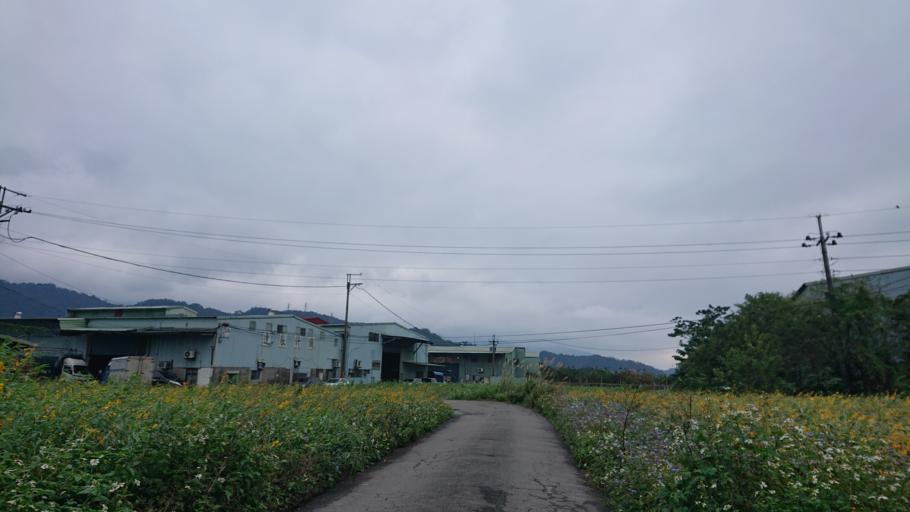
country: TW
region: Taiwan
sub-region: Taoyuan
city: Taoyuan
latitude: 24.9424
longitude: 121.3915
